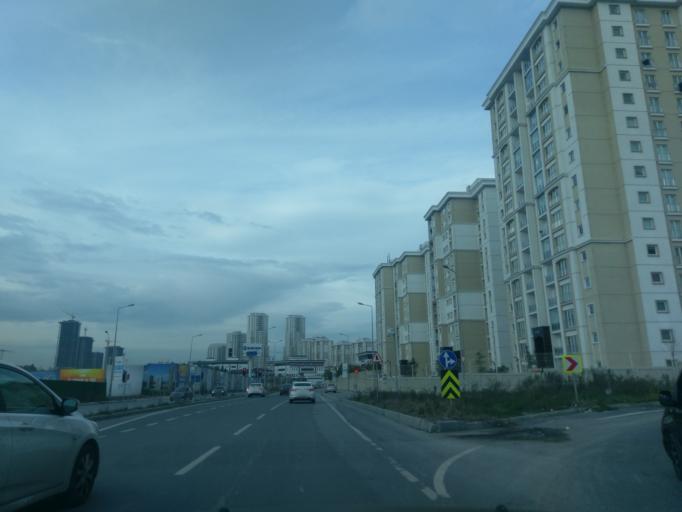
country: TR
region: Istanbul
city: Esenyurt
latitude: 41.0837
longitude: 28.6525
